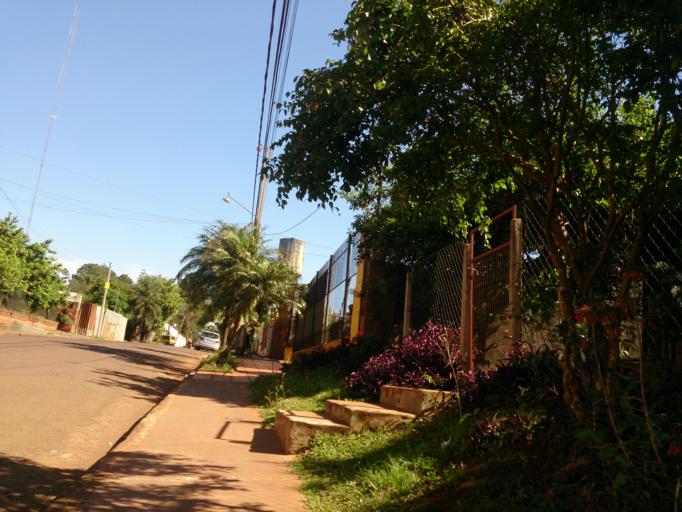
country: AR
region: Misiones
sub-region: Departamento de Obera
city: Obera
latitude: -27.4866
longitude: -55.1092
